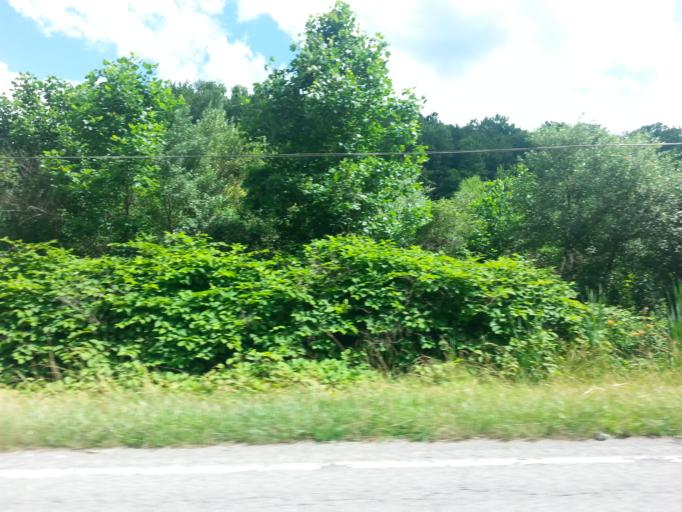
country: US
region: Virginia
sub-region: Lee County
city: Jonesville
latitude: 36.7638
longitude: -83.1793
